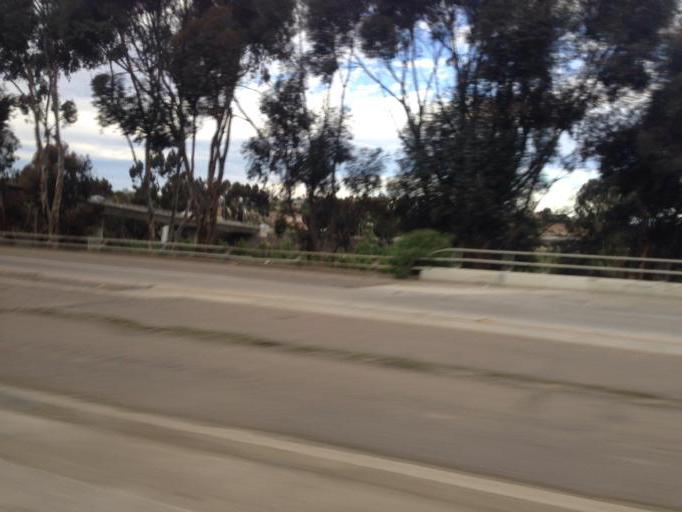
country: US
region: California
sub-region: San Diego County
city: Chula Vista
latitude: 32.6570
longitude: -117.0730
